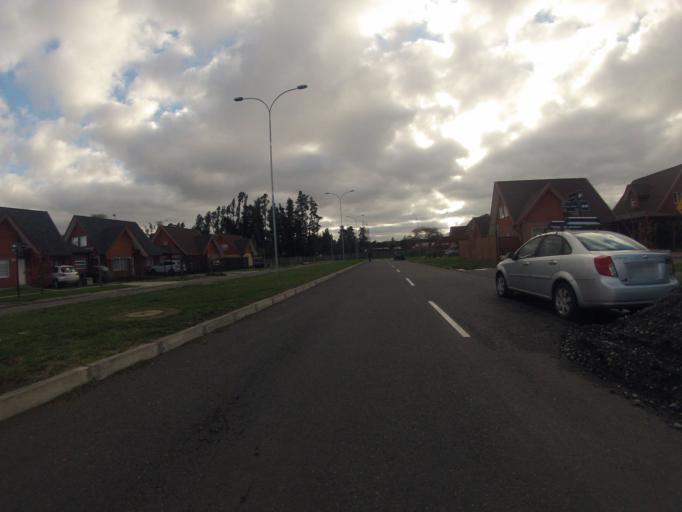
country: CL
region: Araucania
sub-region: Provincia de Cautin
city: Temuco
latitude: -38.7389
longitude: -72.6484
